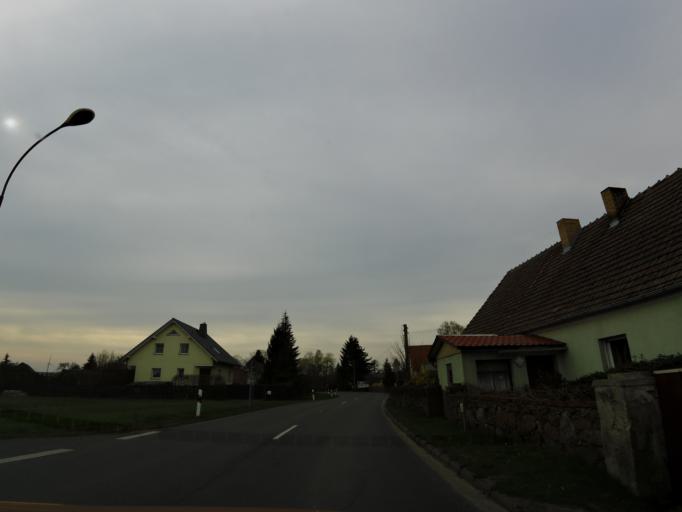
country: DE
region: Brandenburg
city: Tauche
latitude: 52.1719
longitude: 14.2006
